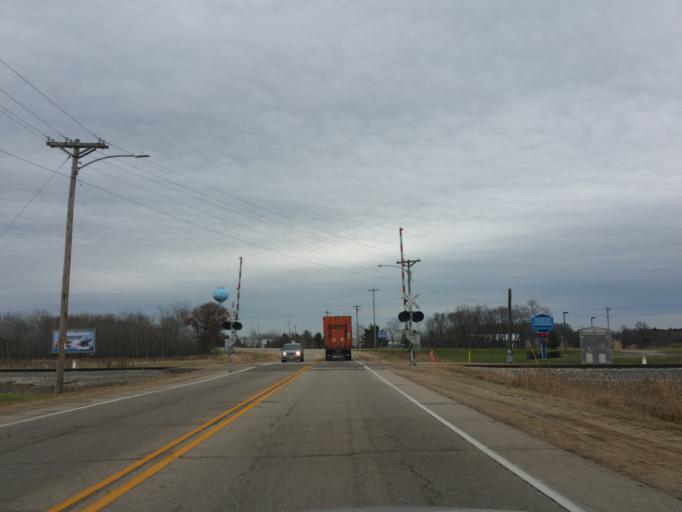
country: US
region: Wisconsin
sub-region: Juneau County
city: New Lisbon
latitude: 43.8811
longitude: -90.1554
